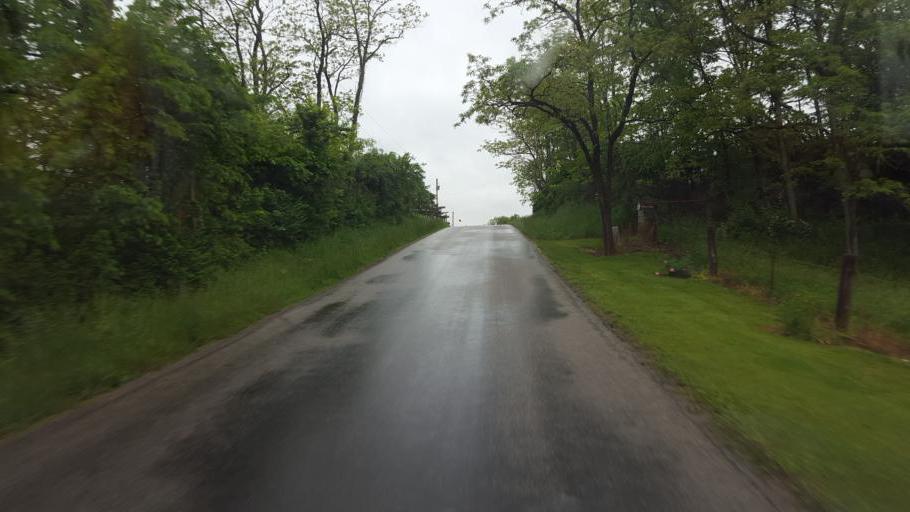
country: US
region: Ohio
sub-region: Medina County
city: Lodi
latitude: 41.0855
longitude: -82.0408
